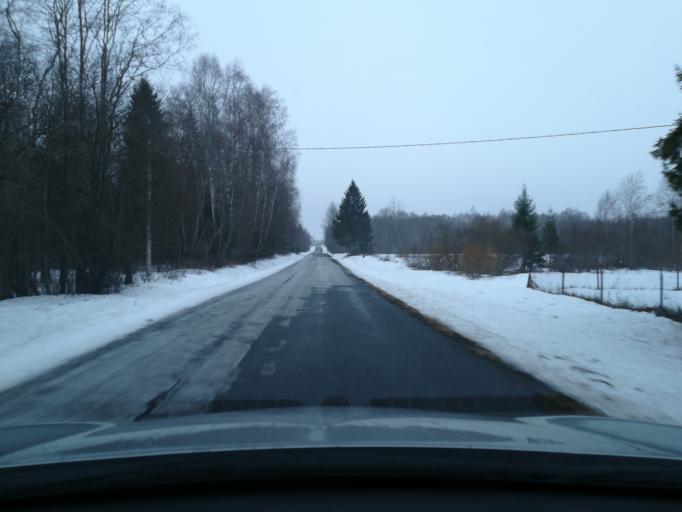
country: EE
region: Harju
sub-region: Raasiku vald
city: Raasiku
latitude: 59.3423
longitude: 25.2455
